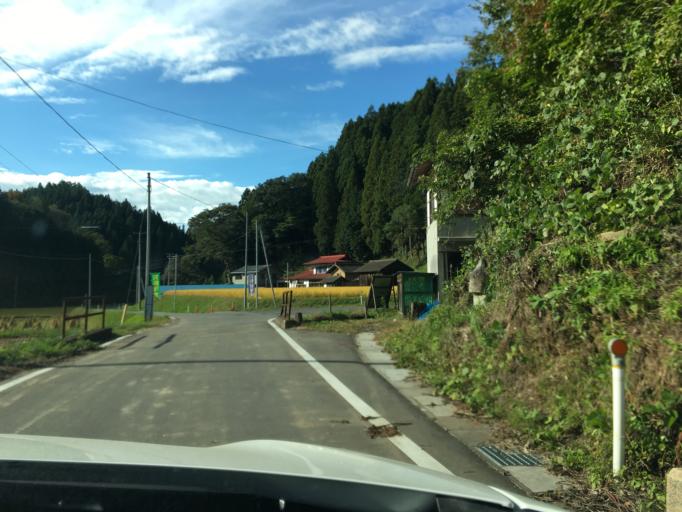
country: JP
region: Fukushima
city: Ishikawa
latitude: 37.1665
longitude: 140.4992
